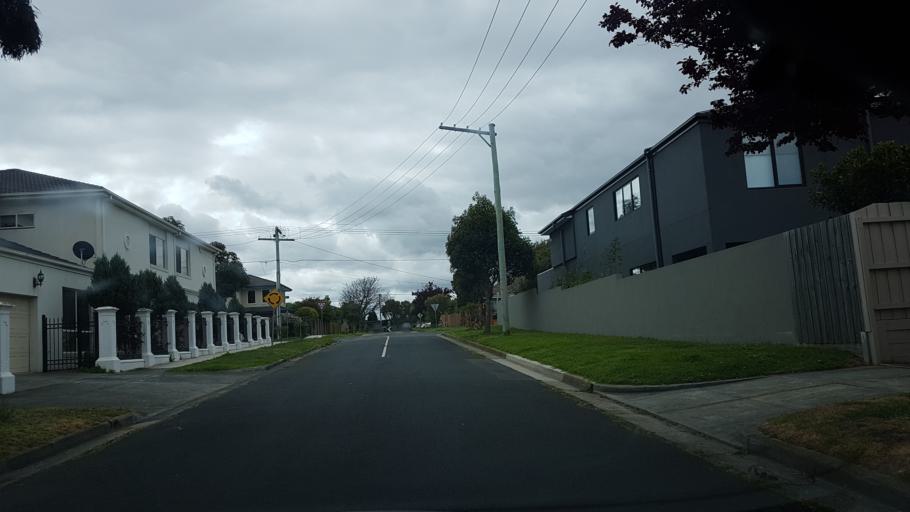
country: AU
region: Victoria
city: McKinnon
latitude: -37.9295
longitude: 145.0468
